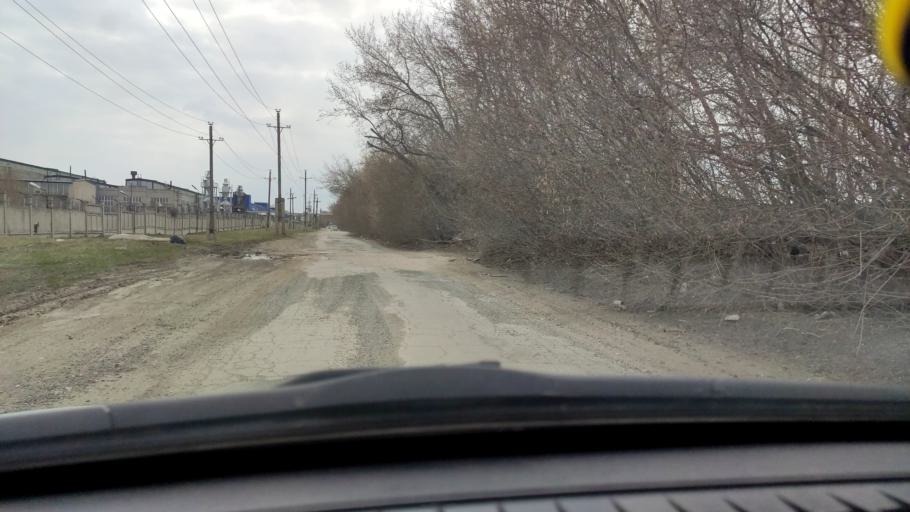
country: RU
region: Samara
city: Tol'yatti
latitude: 53.5263
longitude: 49.4574
